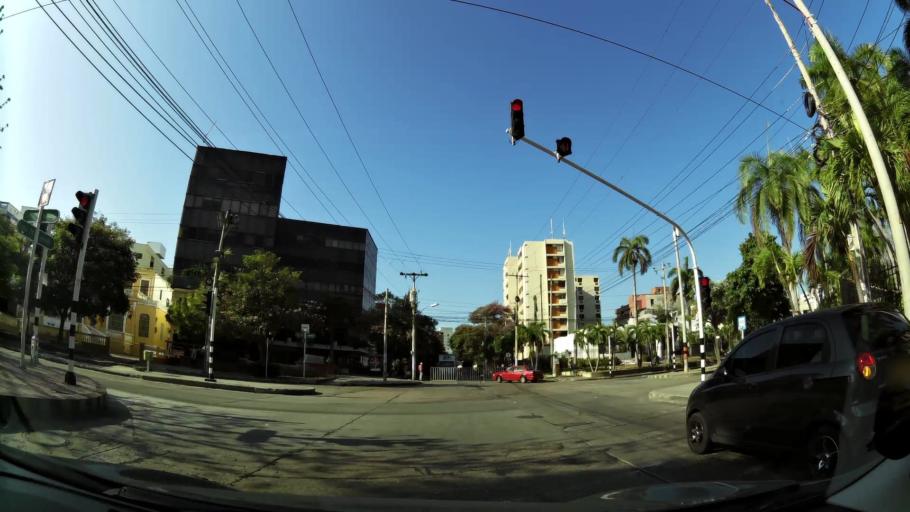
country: CO
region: Atlantico
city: Barranquilla
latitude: 10.9981
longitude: -74.7997
